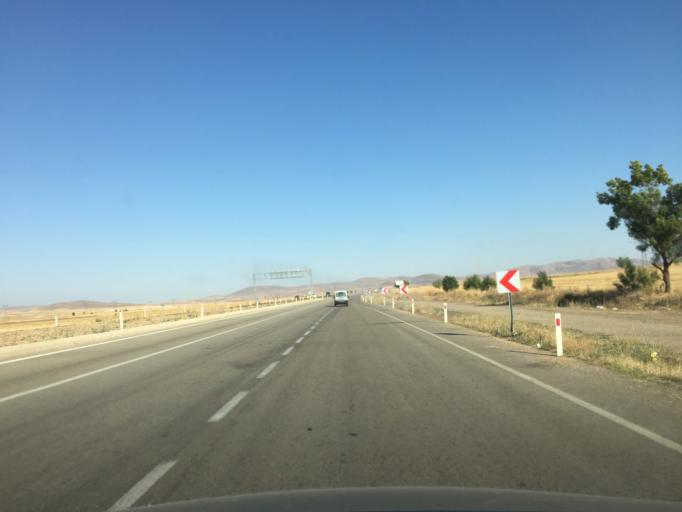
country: TR
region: Kirsehir
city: Akpinar
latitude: 39.3278
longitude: 34.0401
